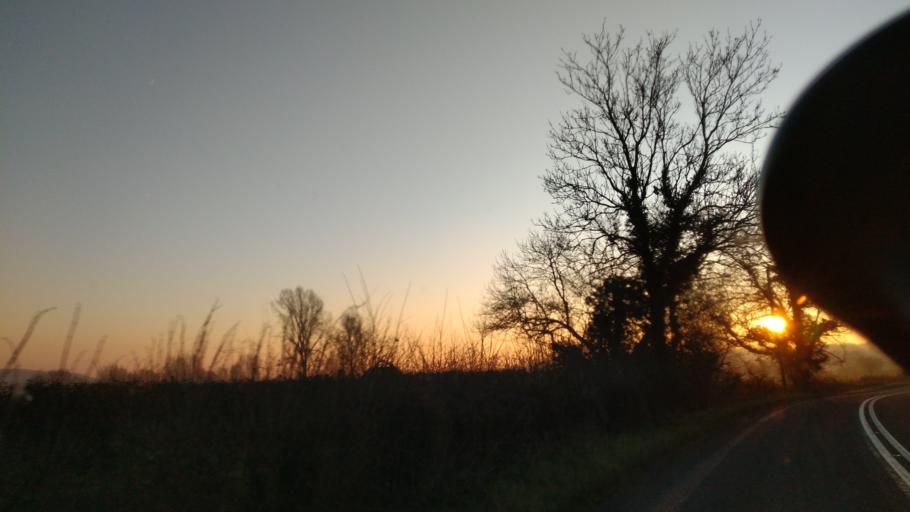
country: GB
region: England
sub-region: Wiltshire
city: Calne
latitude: 51.4183
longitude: -2.0146
